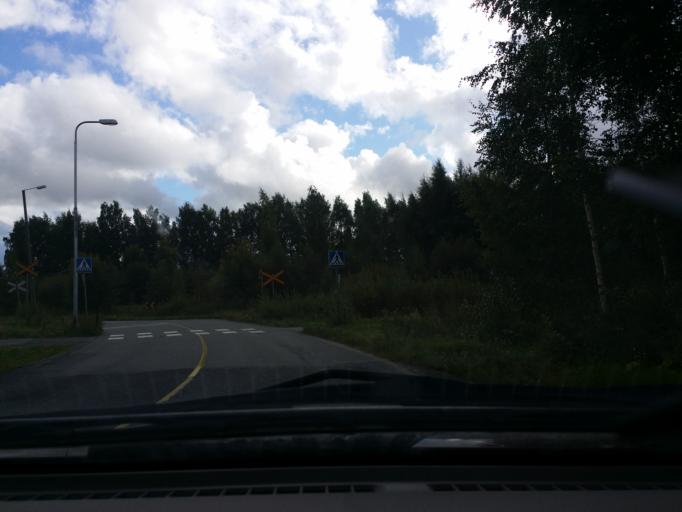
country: FI
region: Satakunta
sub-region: Pori
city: Pori
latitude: 61.4954
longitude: 21.8248
